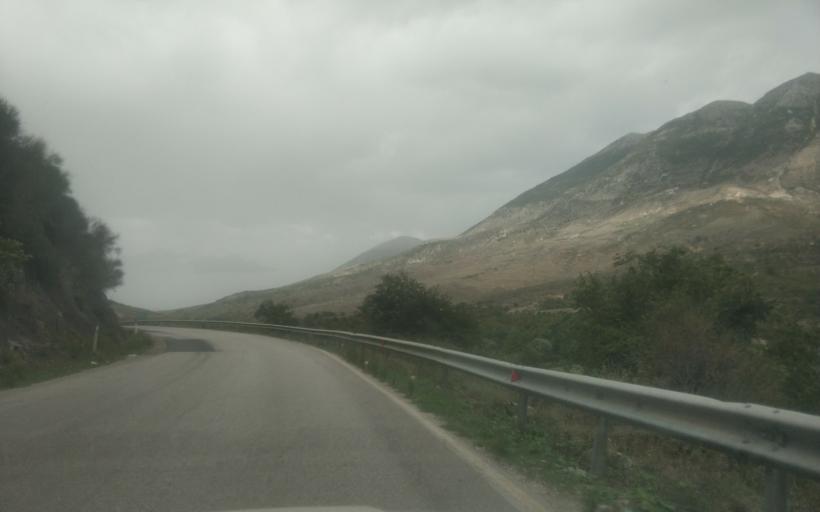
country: AL
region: Gjirokaster
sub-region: Rrethi i Gjirokastres
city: Picar
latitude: 40.2286
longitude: 20.0851
